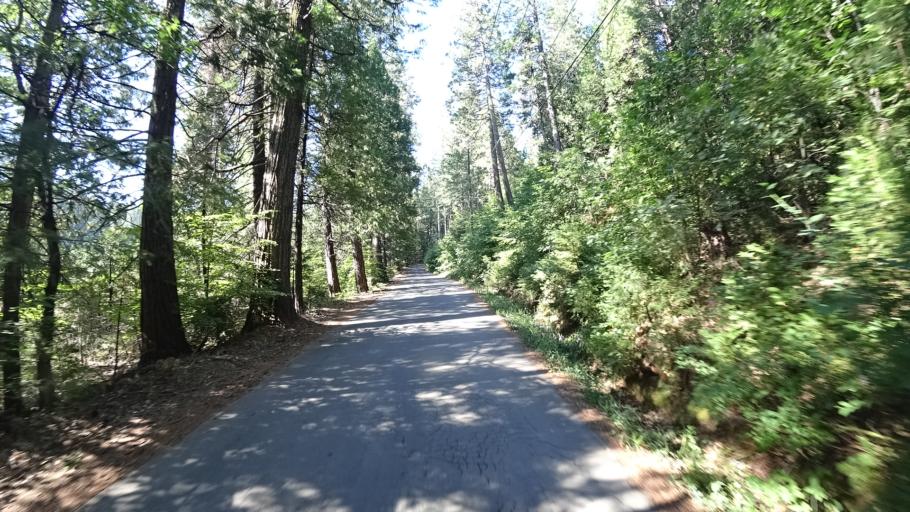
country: US
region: California
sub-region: Calaveras County
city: Arnold
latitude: 38.2622
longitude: -120.3447
